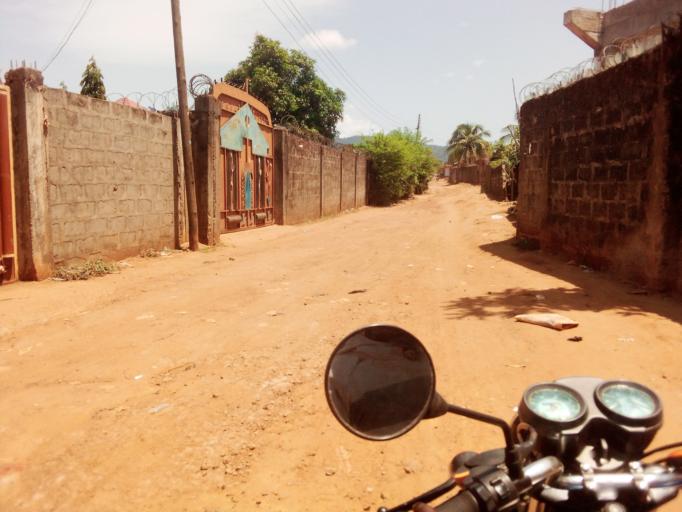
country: SL
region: Western Area
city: Waterloo
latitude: 8.3329
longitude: -13.0743
